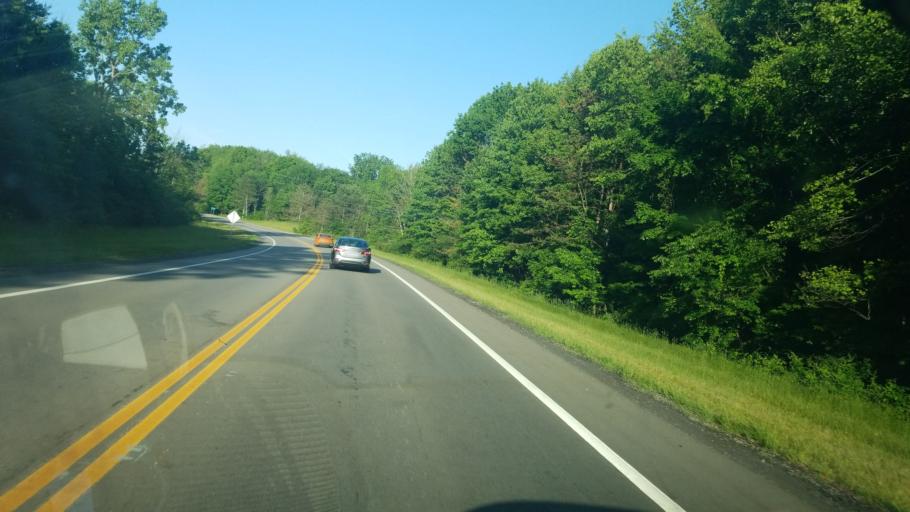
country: US
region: Ohio
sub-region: Portage County
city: Kent
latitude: 41.1346
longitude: -81.3279
